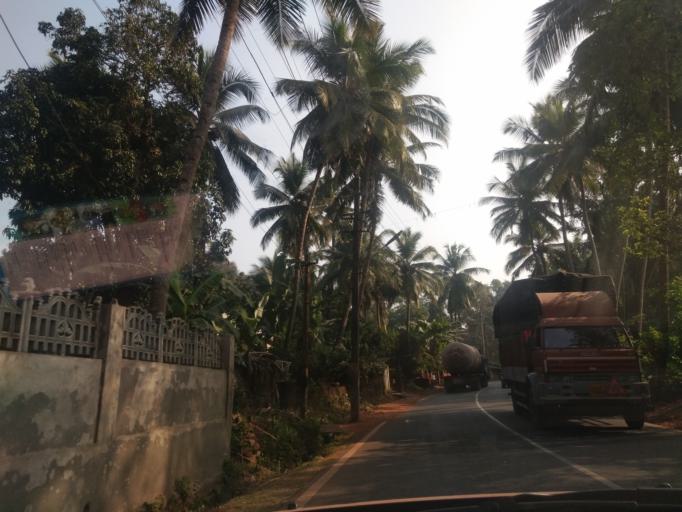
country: IN
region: Goa
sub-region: North Goa
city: Queula
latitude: 15.3678
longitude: 74.0066
